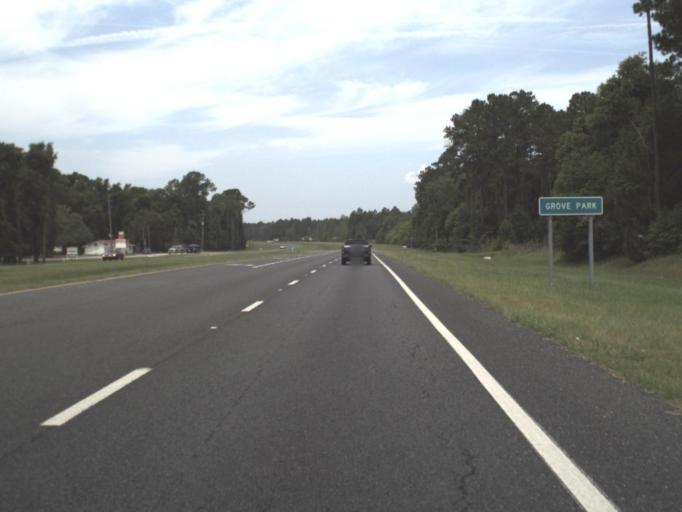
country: US
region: Florida
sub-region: Alachua County
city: Hawthorne
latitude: 29.6008
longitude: -82.1566
